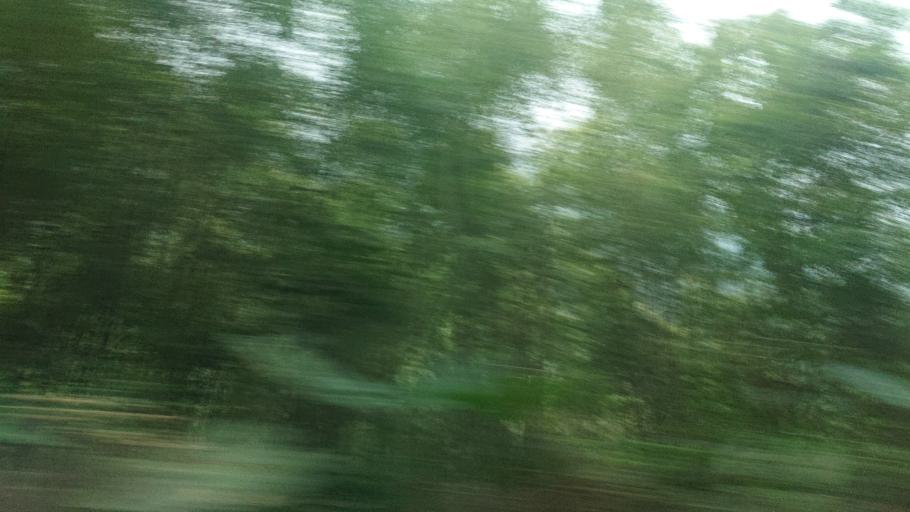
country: TW
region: Taiwan
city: Lugu
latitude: 23.6051
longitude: 120.7117
